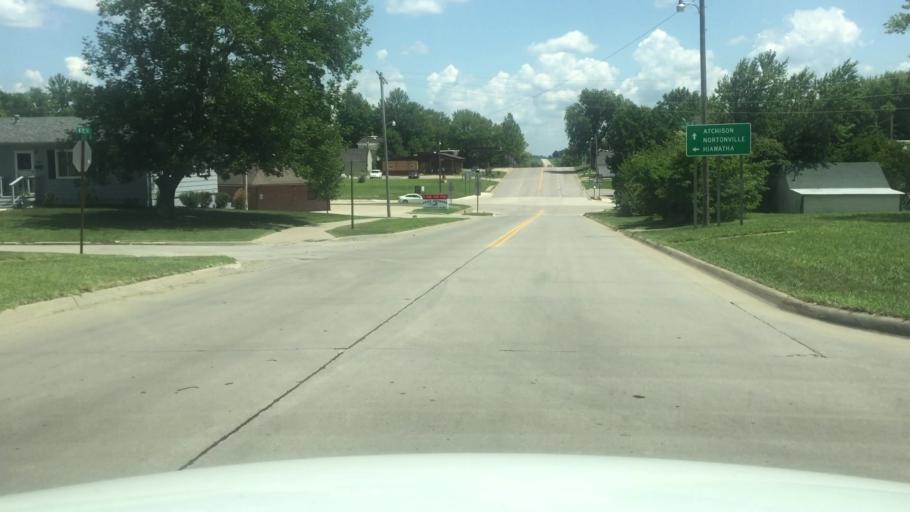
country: US
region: Kansas
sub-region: Brown County
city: Horton
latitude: 39.6673
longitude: -95.5287
